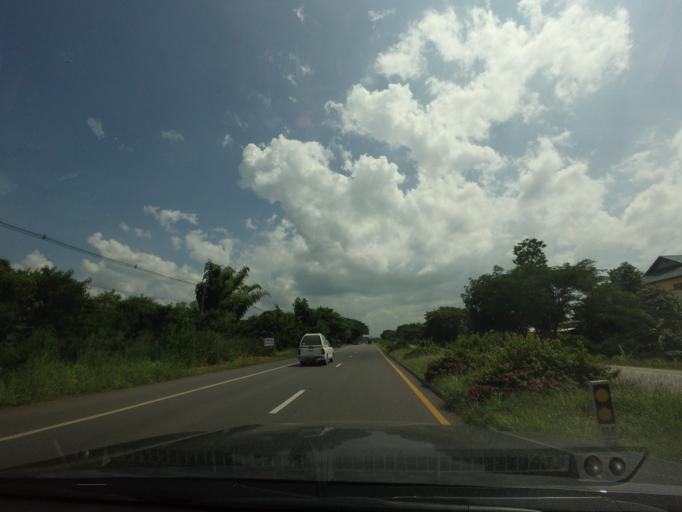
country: TH
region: Phetchabun
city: Phetchabun
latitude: 16.2338
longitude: 101.0824
